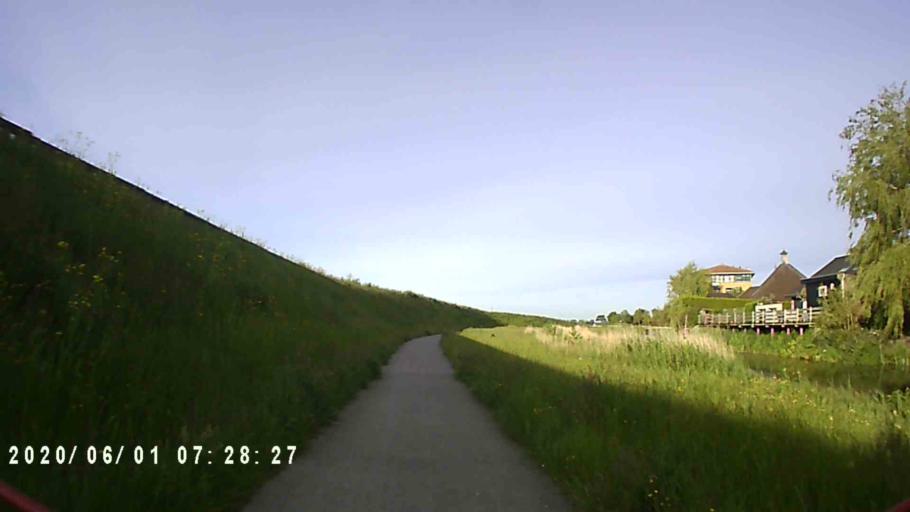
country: NL
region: Friesland
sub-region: Gemeente Dongeradeel
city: Dokkum
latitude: 53.3143
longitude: 6.0147
